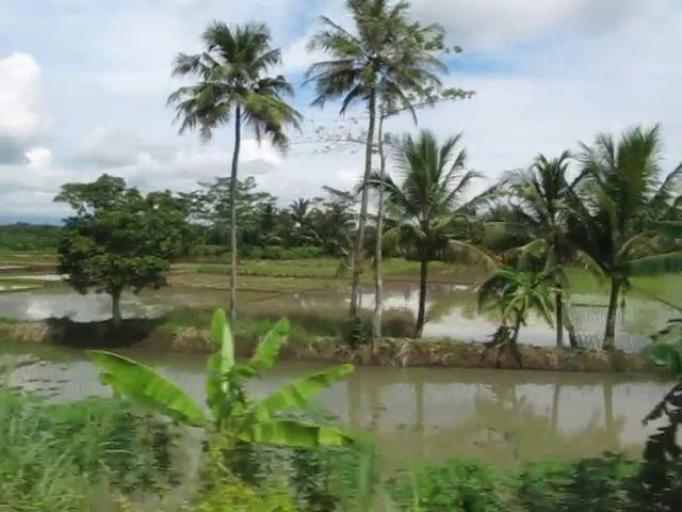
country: ID
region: Central Java
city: Meluwung
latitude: -7.3845
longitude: 108.6939
